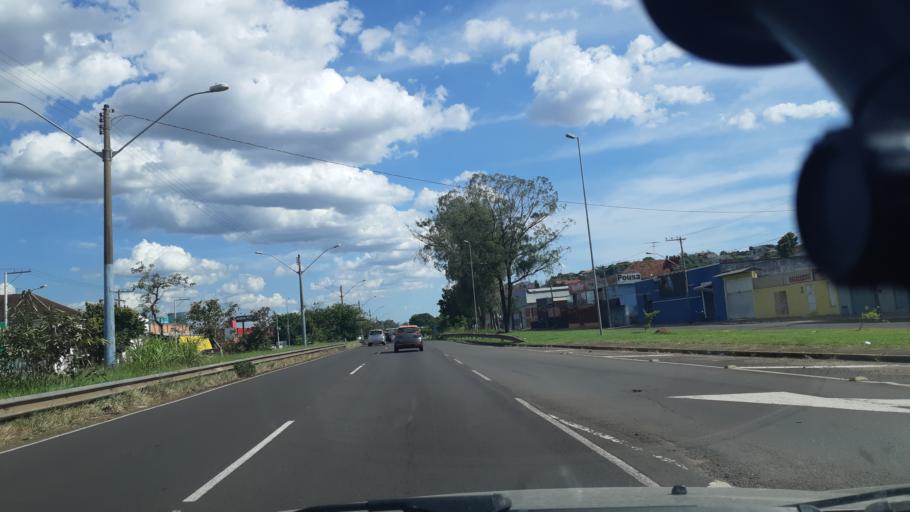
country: BR
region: Rio Grande do Sul
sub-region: Novo Hamburgo
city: Novo Hamburgo
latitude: -29.6736
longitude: -51.1428
